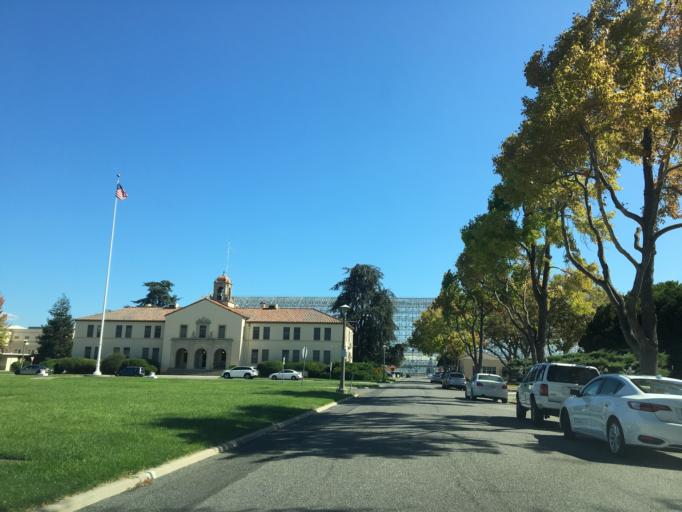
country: US
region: California
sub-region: Santa Clara County
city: Mountain View
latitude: 37.4111
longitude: -122.0587
